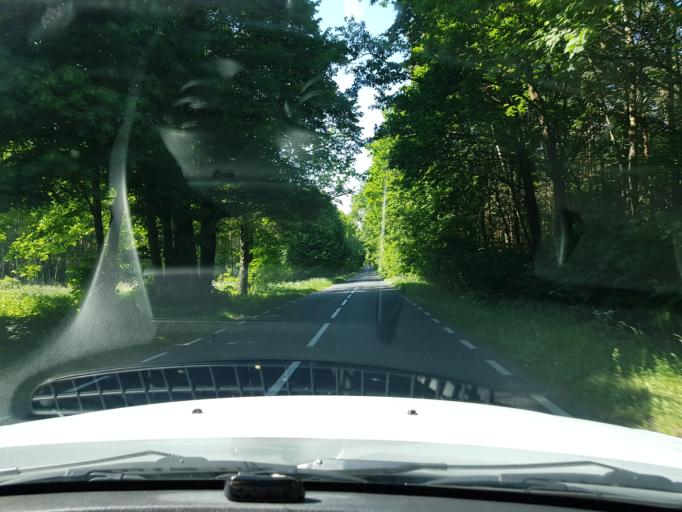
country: PL
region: West Pomeranian Voivodeship
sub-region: Powiat gryfinski
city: Gryfino
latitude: 53.1871
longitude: 14.5344
